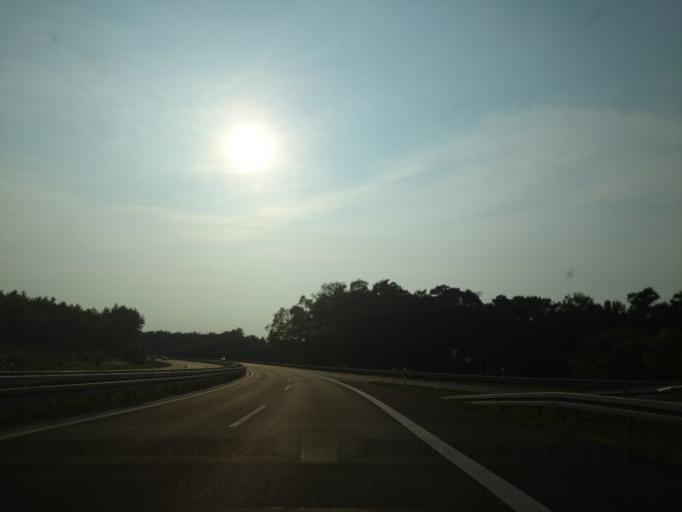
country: DE
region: Berlin
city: Wannsee
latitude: 52.3754
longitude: 13.1663
